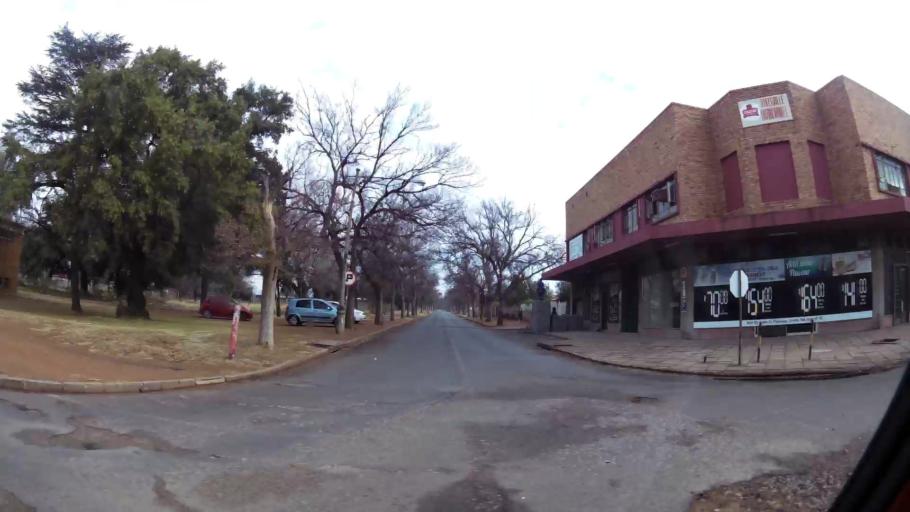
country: ZA
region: Gauteng
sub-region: Sedibeng District Municipality
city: Vanderbijlpark
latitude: -26.6922
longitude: 27.8196
